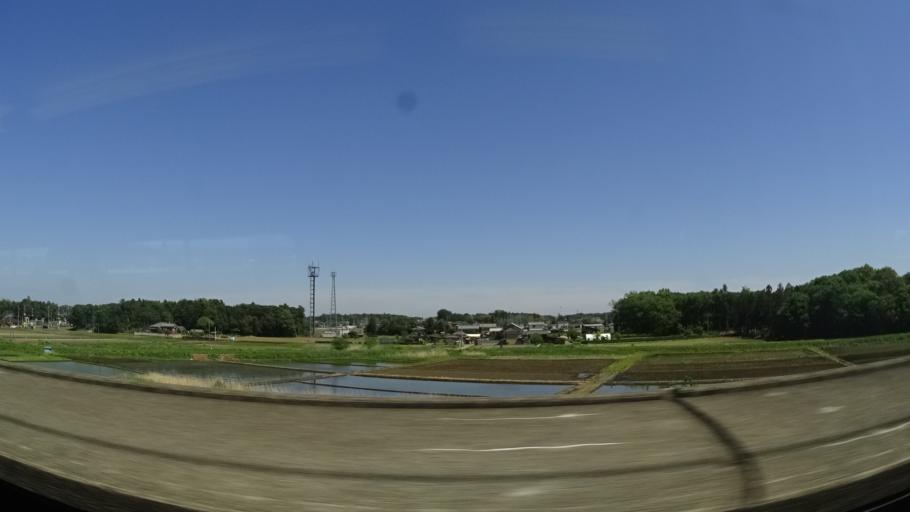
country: JP
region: Ibaraki
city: Koga
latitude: 36.1682
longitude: 139.7344
